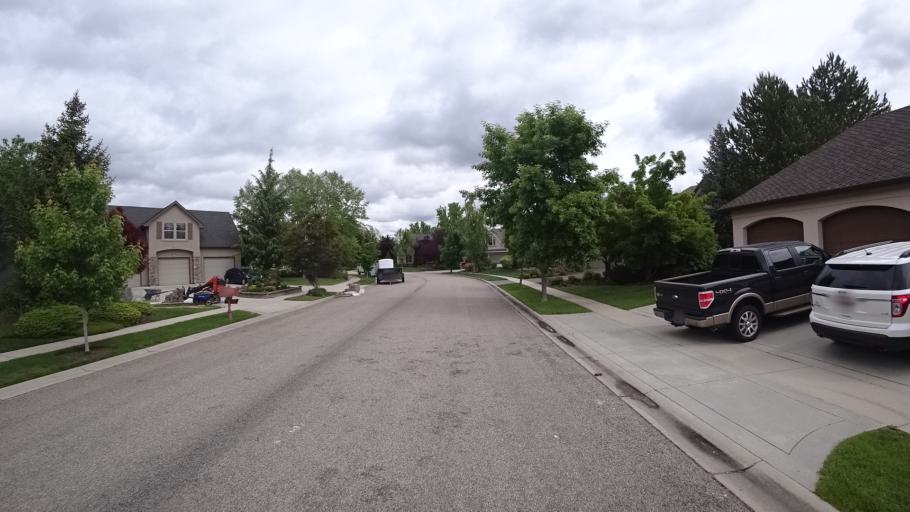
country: US
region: Idaho
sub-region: Ada County
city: Eagle
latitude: 43.6816
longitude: -116.3605
